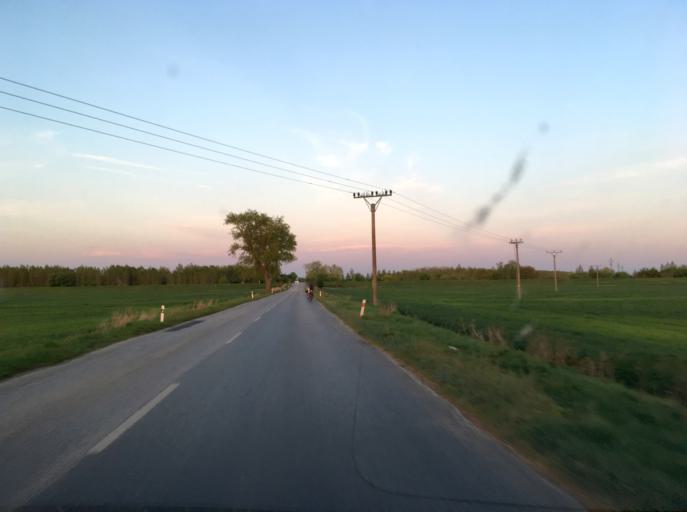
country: SK
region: Nitriansky
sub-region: Okres Nove Zamky
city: Nove Zamky
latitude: 47.9226
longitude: 18.1022
